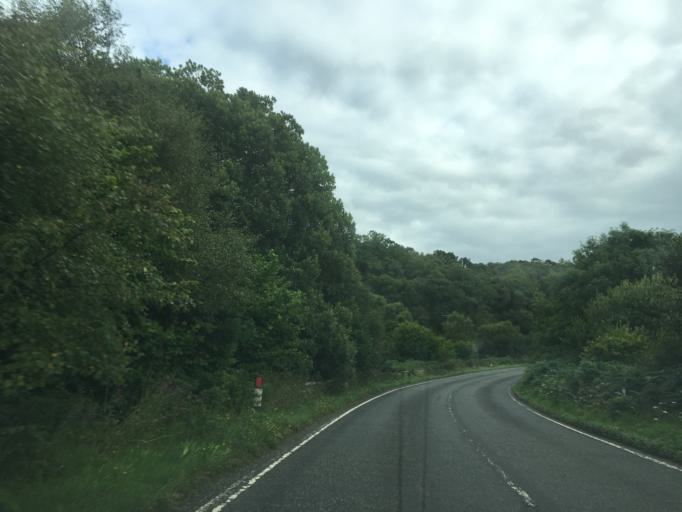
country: GB
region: Scotland
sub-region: Argyll and Bute
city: Oban
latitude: 56.3369
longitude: -5.5130
